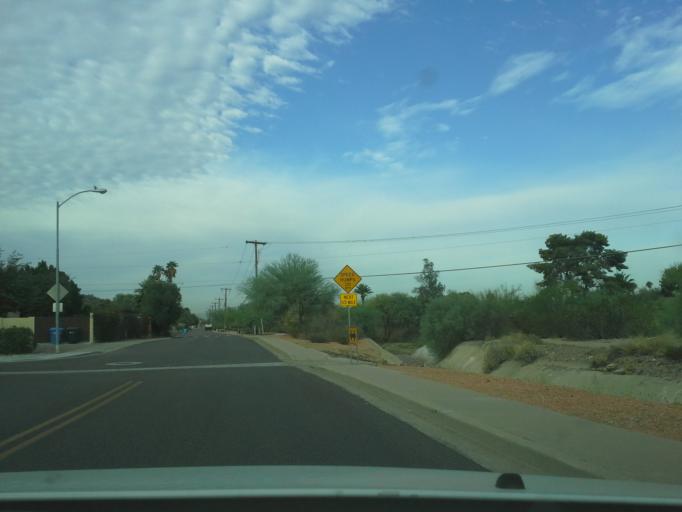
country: US
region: Arizona
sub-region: Maricopa County
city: Glendale
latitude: 33.6038
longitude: -112.0905
